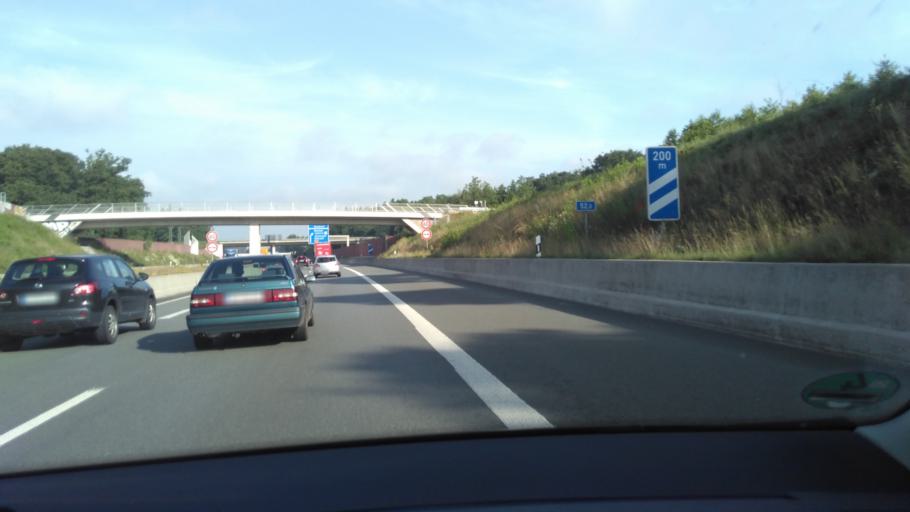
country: DE
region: North Rhine-Westphalia
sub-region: Regierungsbezirk Detmold
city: Bielefeld
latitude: 51.9696
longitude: 8.4914
